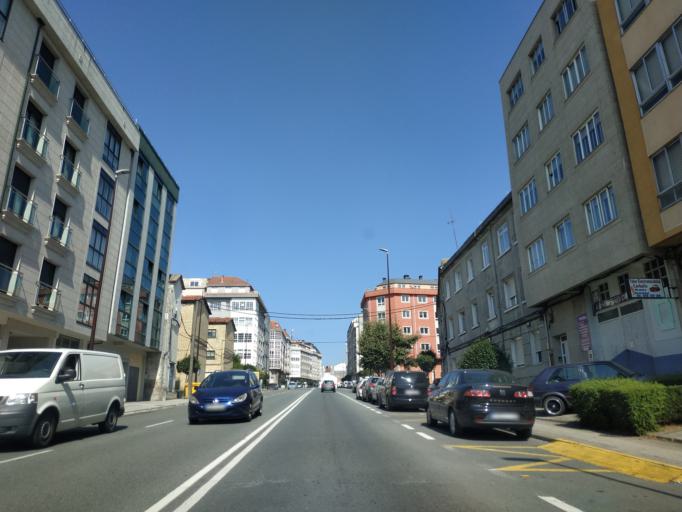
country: ES
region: Galicia
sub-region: Provincia da Coruna
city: Carballo
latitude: 43.2185
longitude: -8.6877
